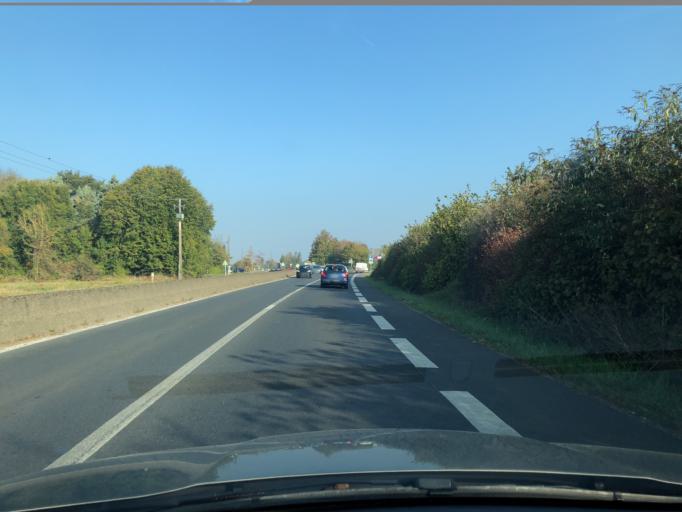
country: FR
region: Centre
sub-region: Departement d'Indre-et-Loire
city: Chanceaux-sur-Choisille
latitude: 47.4480
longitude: 0.6981
